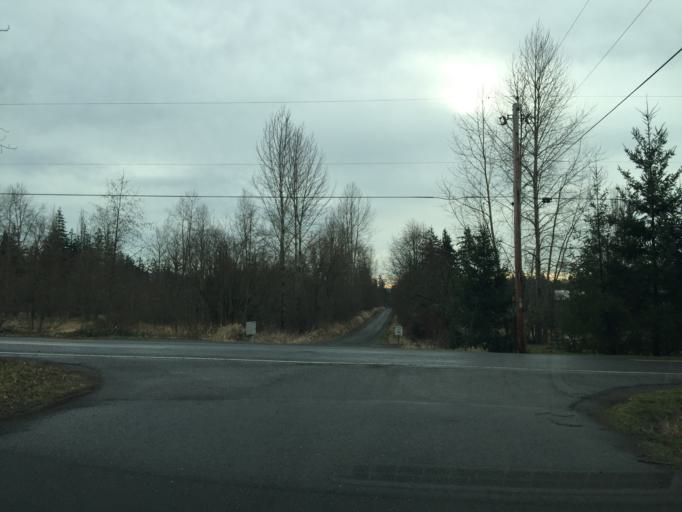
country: US
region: Washington
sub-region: Whatcom County
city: Geneva
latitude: 48.8043
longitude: -122.4317
